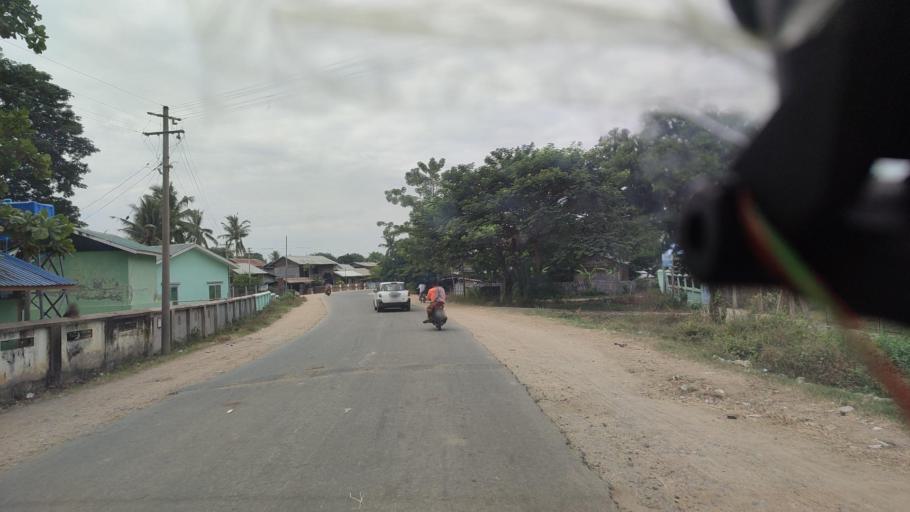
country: MM
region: Mandalay
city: Pyinmana
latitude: 19.7556
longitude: 96.2905
